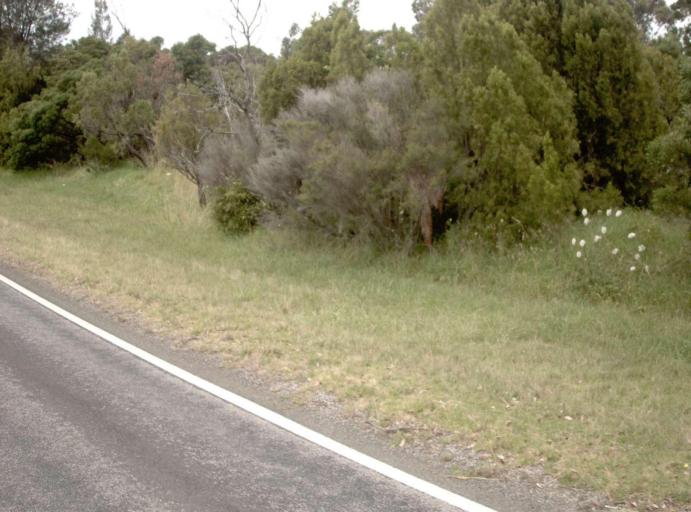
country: AU
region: Victoria
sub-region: Cardinia
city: Pakenham Upper
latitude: -38.0658
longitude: 145.5016
